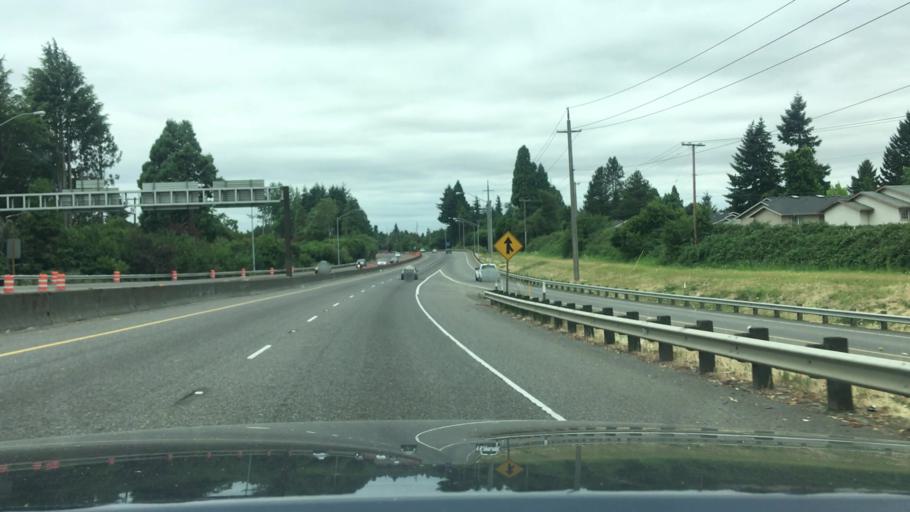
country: US
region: Oregon
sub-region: Lane County
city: Eugene
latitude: 44.0972
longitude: -123.1313
